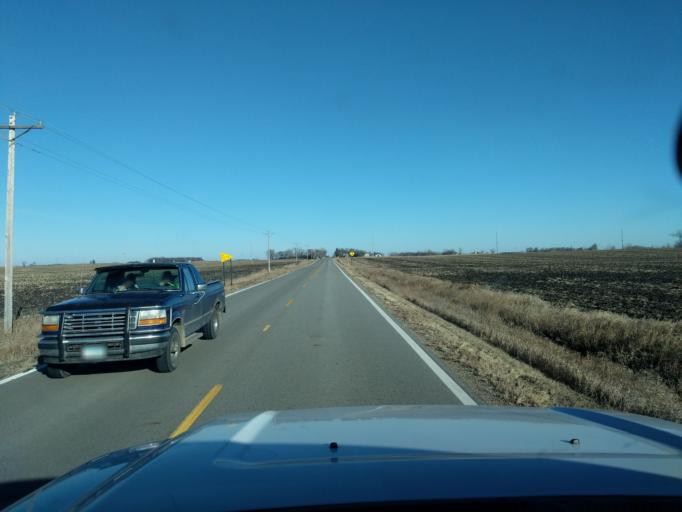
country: US
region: Minnesota
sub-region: Yellow Medicine County
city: Granite Falls
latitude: 44.7854
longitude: -95.4017
